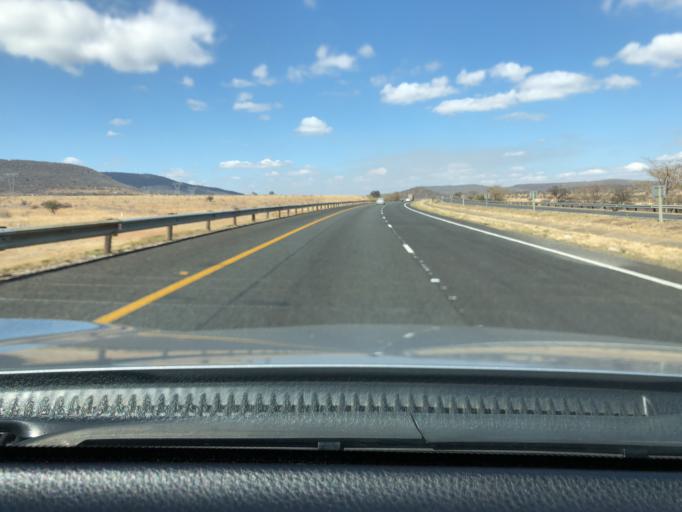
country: ZA
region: KwaZulu-Natal
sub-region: uThukela District Municipality
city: Ladysmith
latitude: -28.6976
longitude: 29.6398
